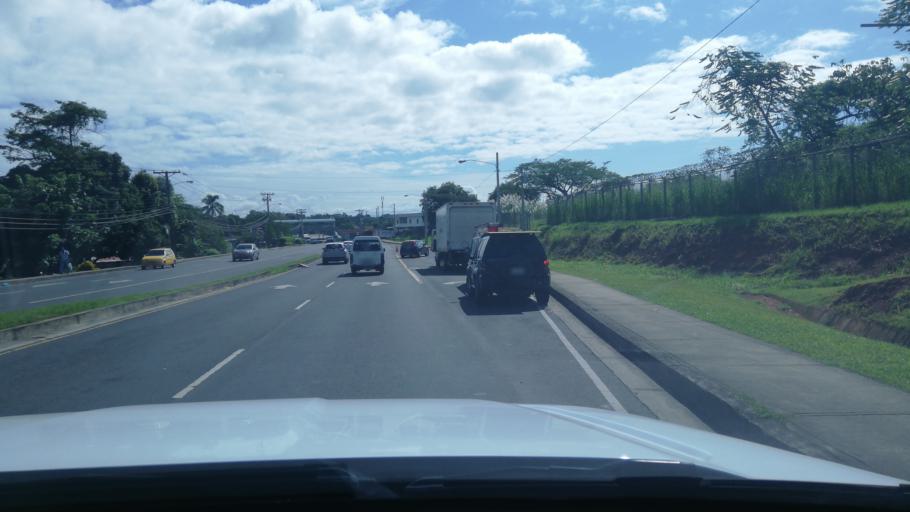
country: PA
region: Panama
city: Tocumen
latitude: 9.0972
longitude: -79.3740
